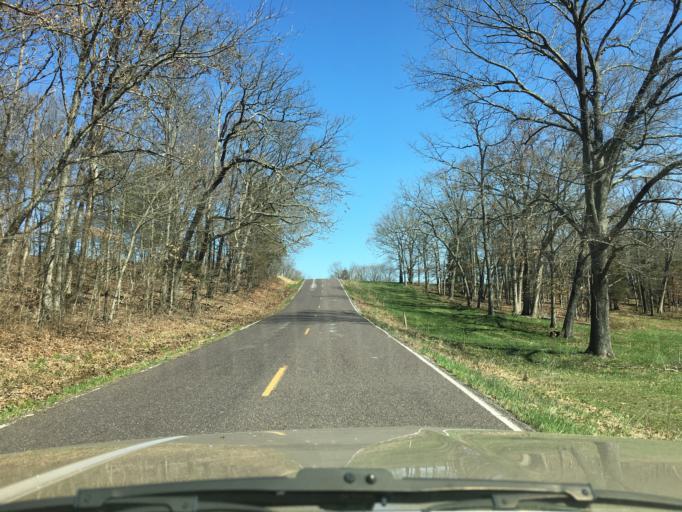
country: US
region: Missouri
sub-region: Franklin County
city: New Haven
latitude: 38.5432
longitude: -91.3303
